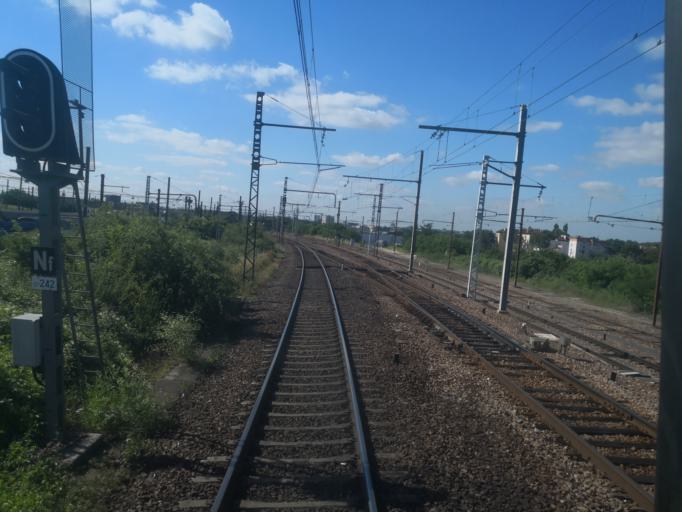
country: FR
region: Ile-de-France
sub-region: Departement de Seine-et-Marne
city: Melun
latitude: 48.5228
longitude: 2.6643
